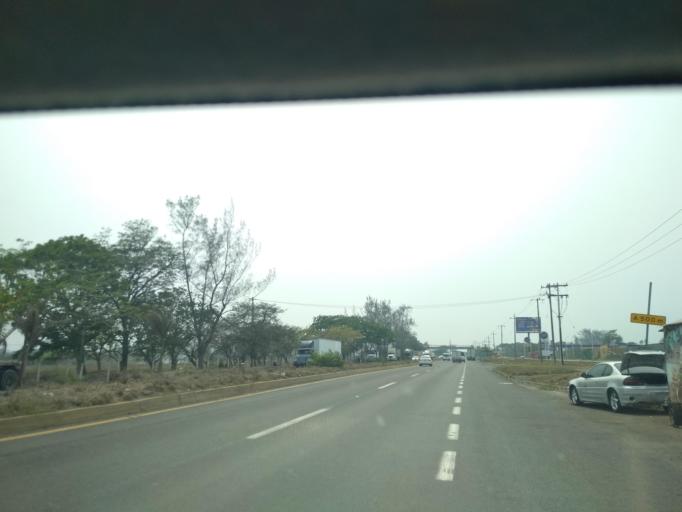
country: MX
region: Veracruz
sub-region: Veracruz
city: Delfino Victoria (Santa Fe)
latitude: 19.1827
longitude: -96.2580
